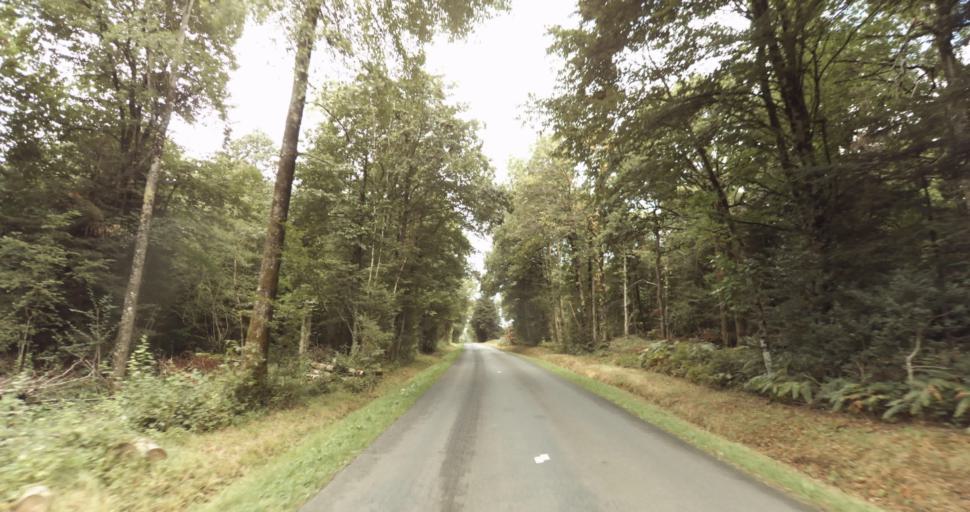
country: FR
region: Lower Normandy
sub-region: Departement de l'Orne
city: Gace
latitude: 48.8007
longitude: 0.2573
